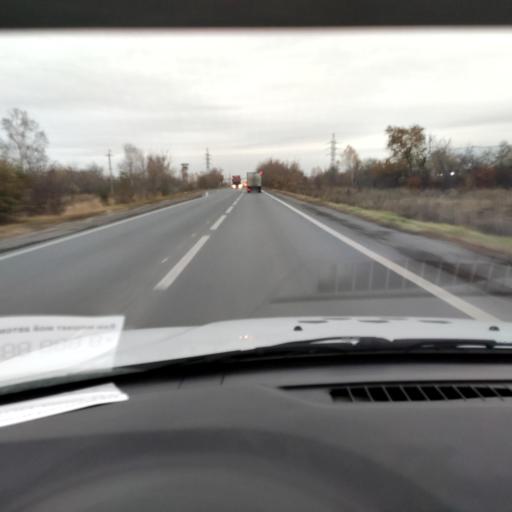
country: RU
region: Samara
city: Tol'yatti
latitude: 53.5480
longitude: 49.3763
